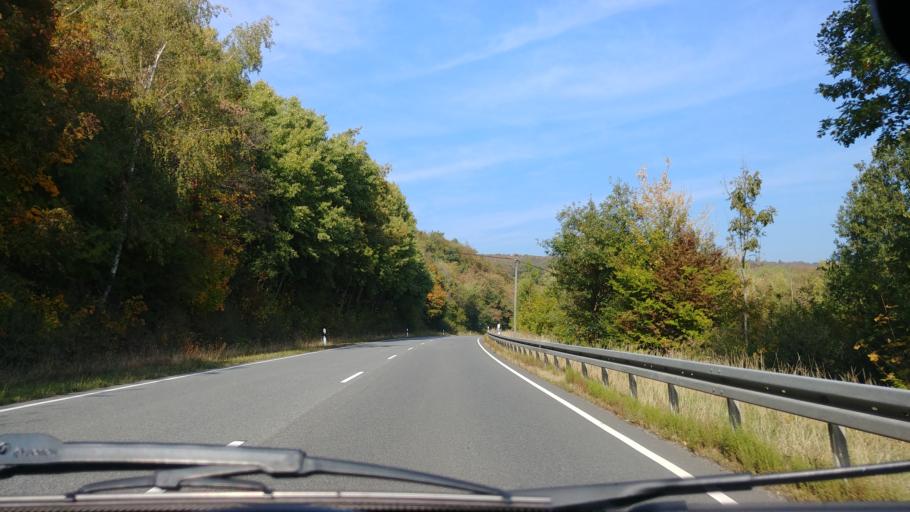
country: DE
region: Hesse
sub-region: Regierungsbezirk Darmstadt
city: Niedernhausen
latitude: 50.1354
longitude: 8.2915
